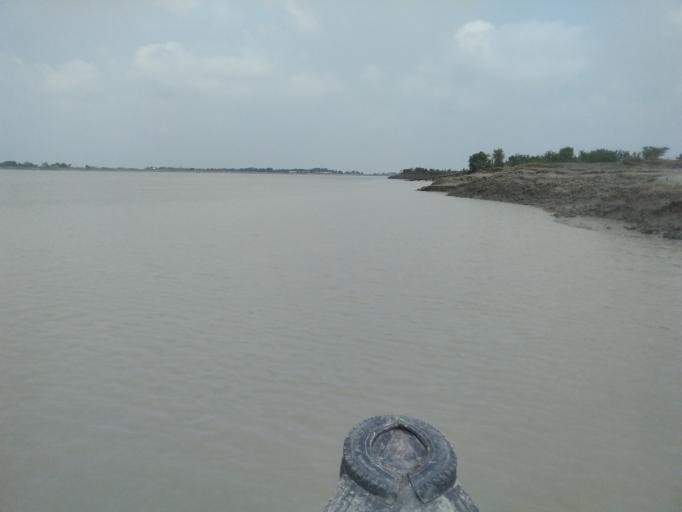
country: BD
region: Khulna
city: Phultala
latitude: 22.6463
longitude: 89.4104
